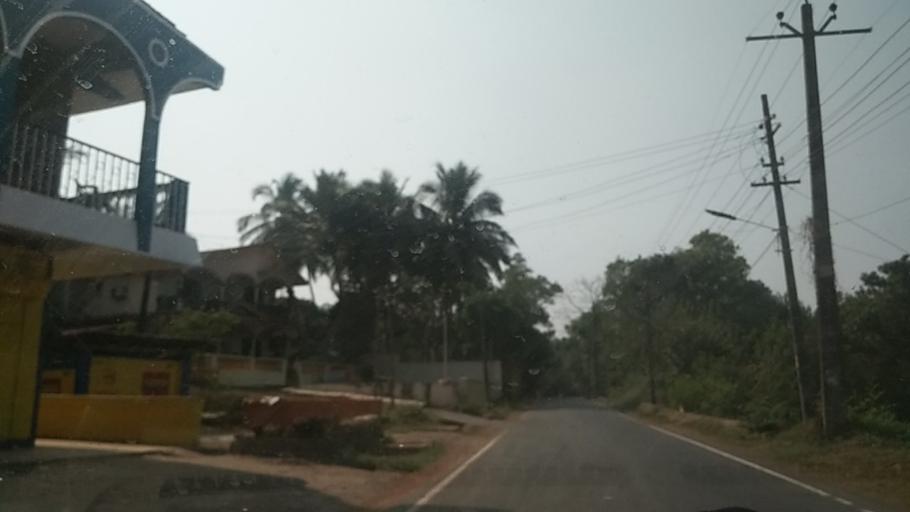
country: IN
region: Goa
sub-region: South Goa
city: Cortalim
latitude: 15.3946
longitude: 73.9319
